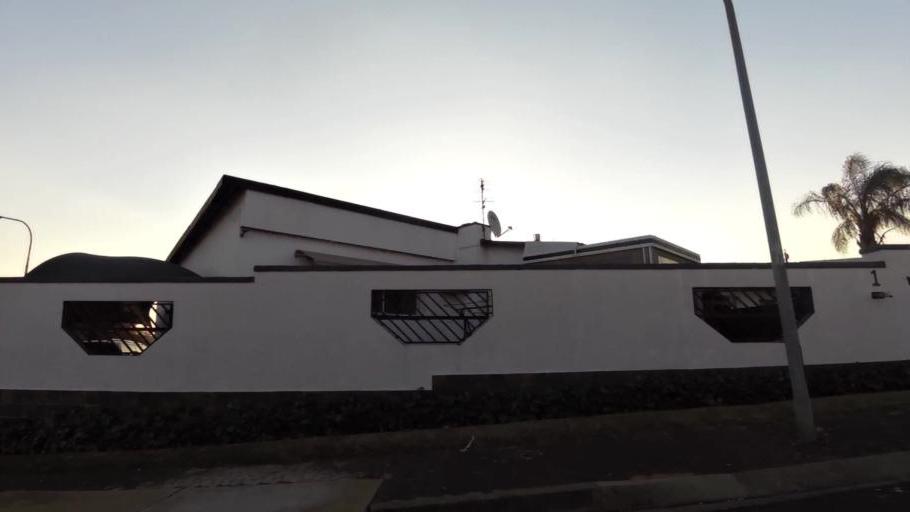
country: ZA
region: Gauteng
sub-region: City of Johannesburg Metropolitan Municipality
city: Roodepoort
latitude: -26.1827
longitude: 27.9477
